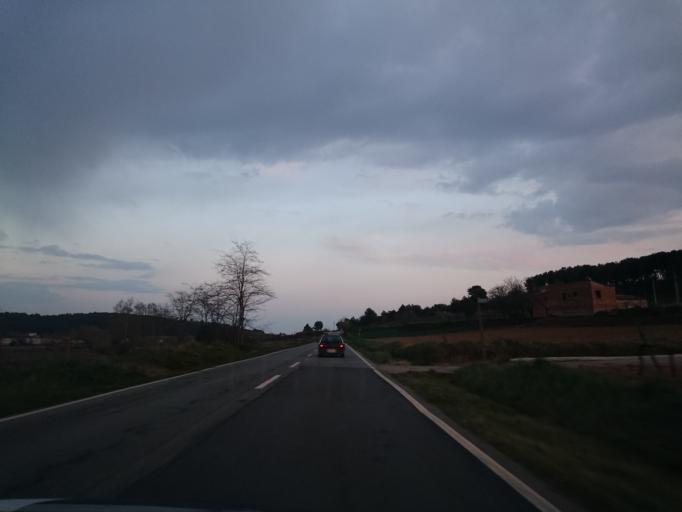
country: ES
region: Catalonia
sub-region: Provincia de Barcelona
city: Vilobi del Penedes
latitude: 41.3654
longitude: 1.6564
